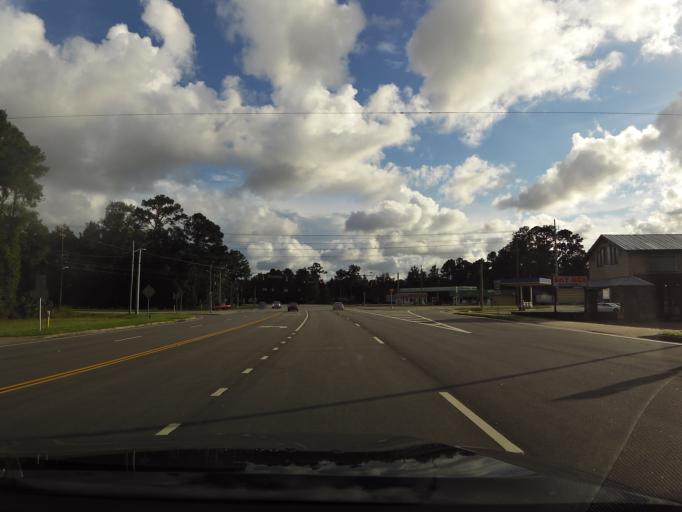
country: US
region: Georgia
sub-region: Liberty County
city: Midway
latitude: 31.8007
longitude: -81.4327
